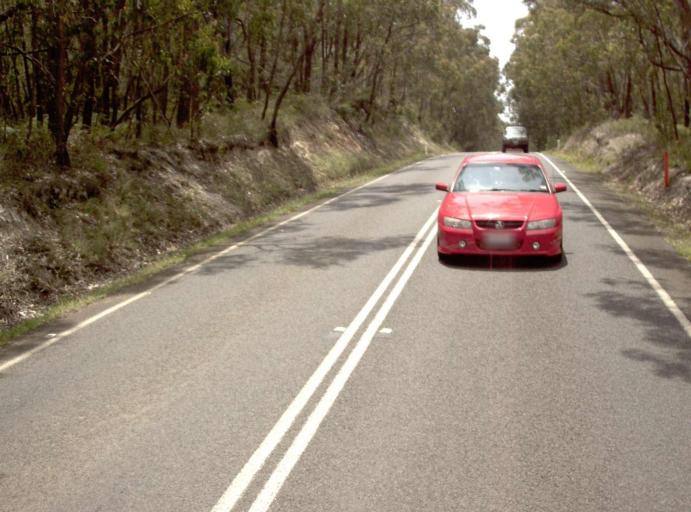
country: AU
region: Victoria
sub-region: Latrobe
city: Traralgon
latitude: -38.4111
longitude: 146.7502
